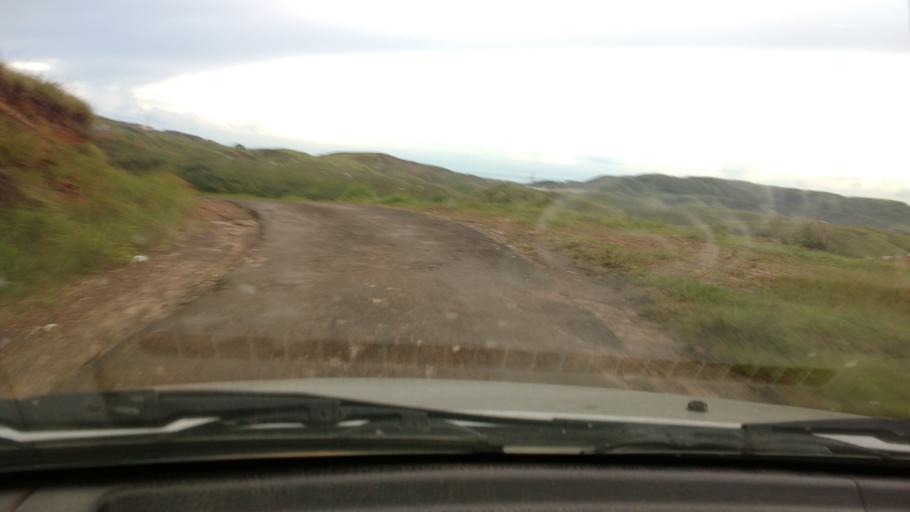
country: IN
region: Meghalaya
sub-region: East Khasi Hills
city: Cherrapunji
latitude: 25.2827
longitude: 91.7069
